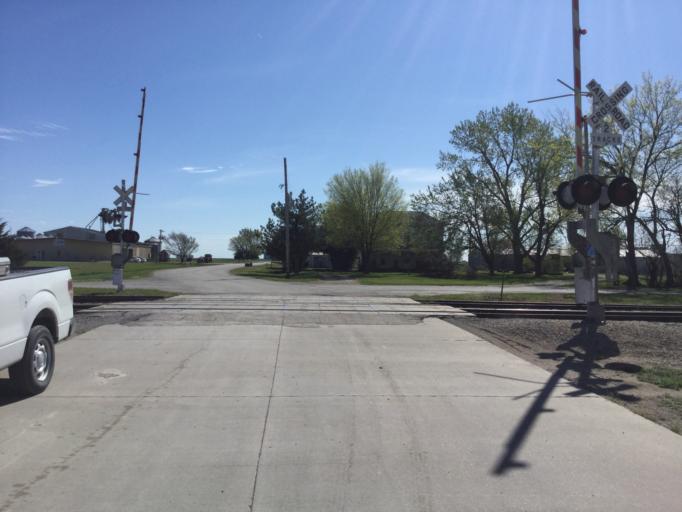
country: US
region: Kansas
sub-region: Neosho County
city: Chanute
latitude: 37.4879
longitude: -95.4703
